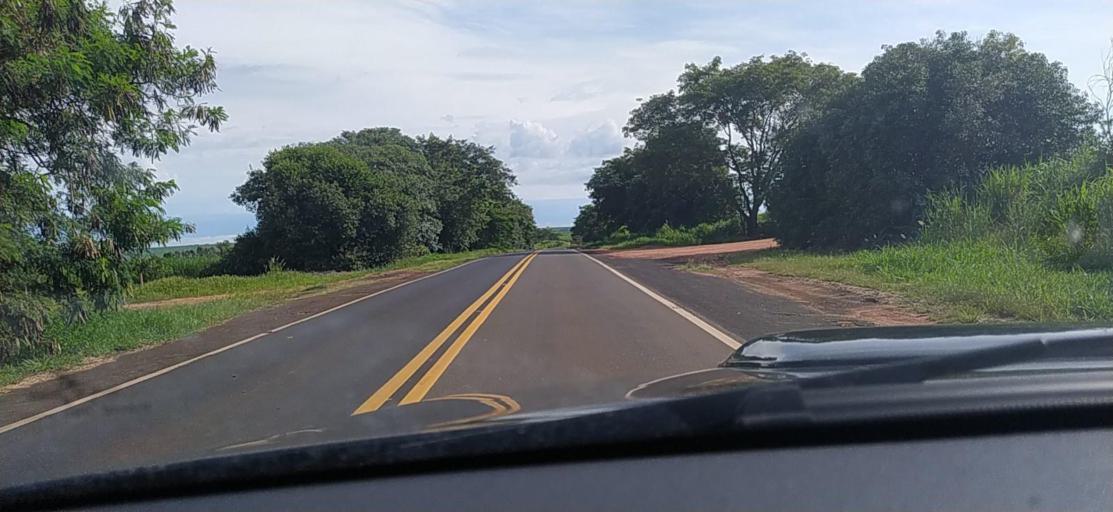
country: BR
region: Sao Paulo
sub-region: Catanduva
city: Catanduva
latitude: -21.0795
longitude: -49.0703
